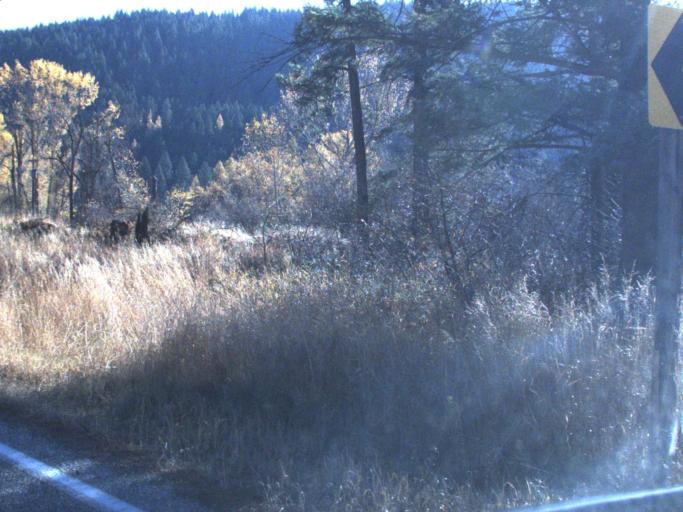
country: CA
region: British Columbia
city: Grand Forks
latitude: 48.9558
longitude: -118.5382
